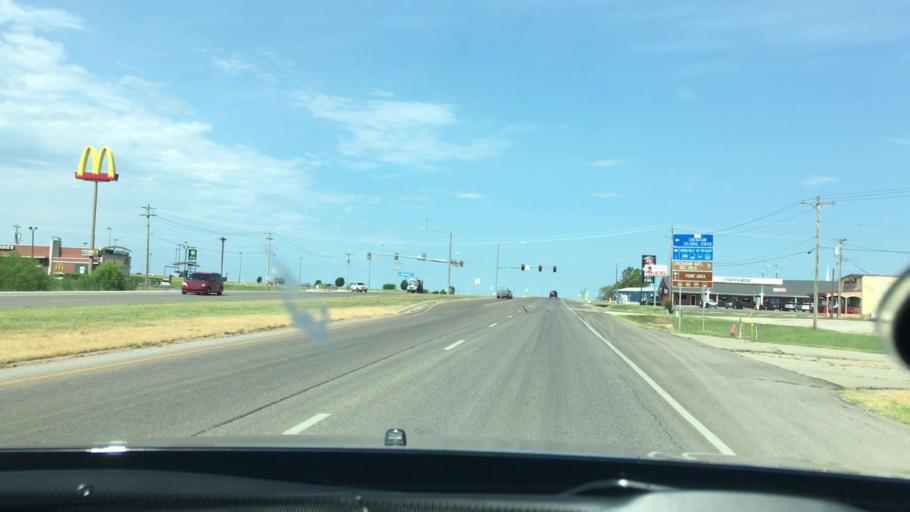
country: US
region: Oklahoma
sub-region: Murray County
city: Sulphur
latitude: 34.5064
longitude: -97.0012
